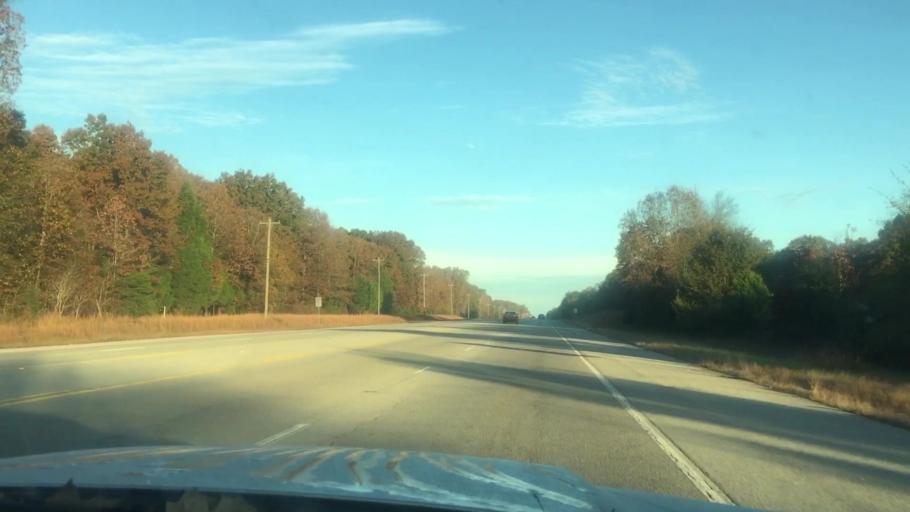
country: US
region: Tennessee
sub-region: Franklin County
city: Estill Springs
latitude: 35.3062
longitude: -86.1593
